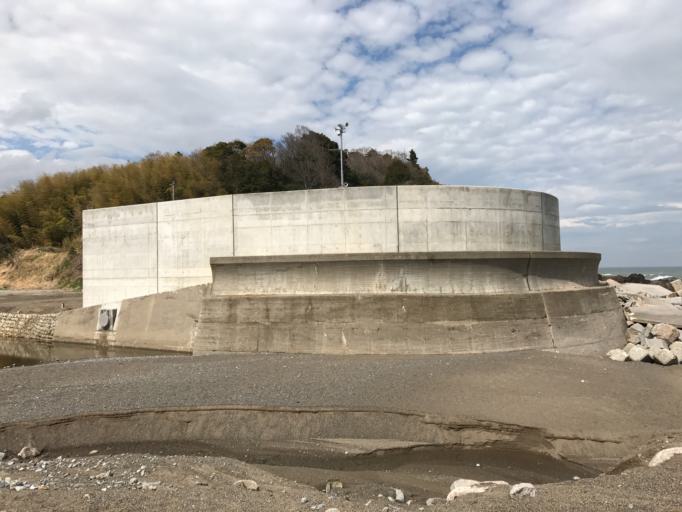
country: JP
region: Fukushima
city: Iwaki
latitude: 37.1555
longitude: 141.0003
